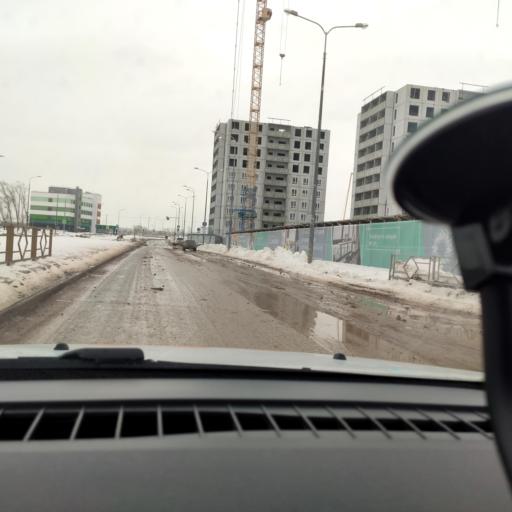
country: RU
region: Samara
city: Samara
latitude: 53.0994
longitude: 50.1738
